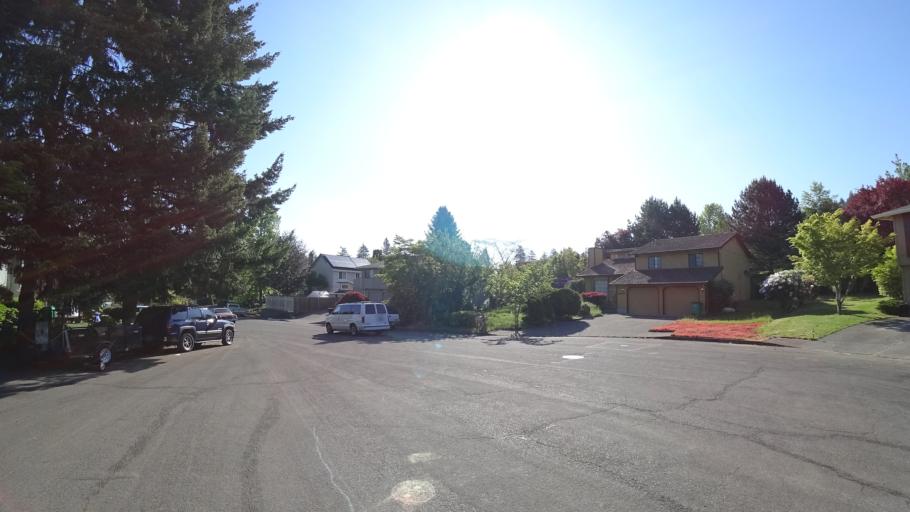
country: US
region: Oregon
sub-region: Multnomah County
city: Lents
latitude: 45.4729
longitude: -122.5457
